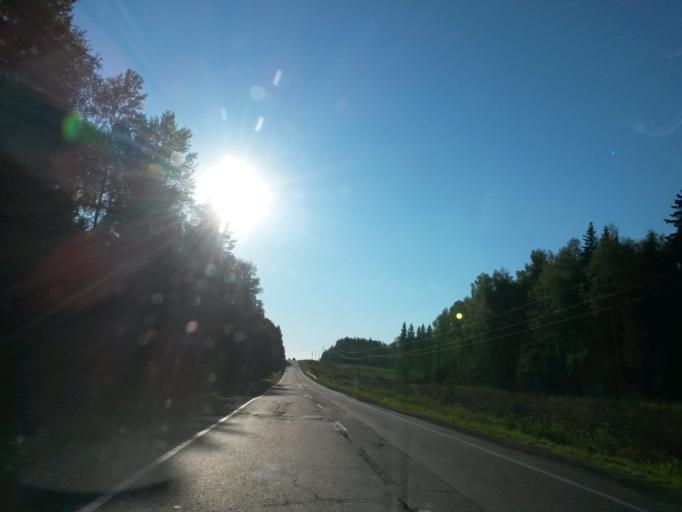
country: RU
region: Jaroslavl
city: Dubki
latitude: 57.2600
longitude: 40.0580
